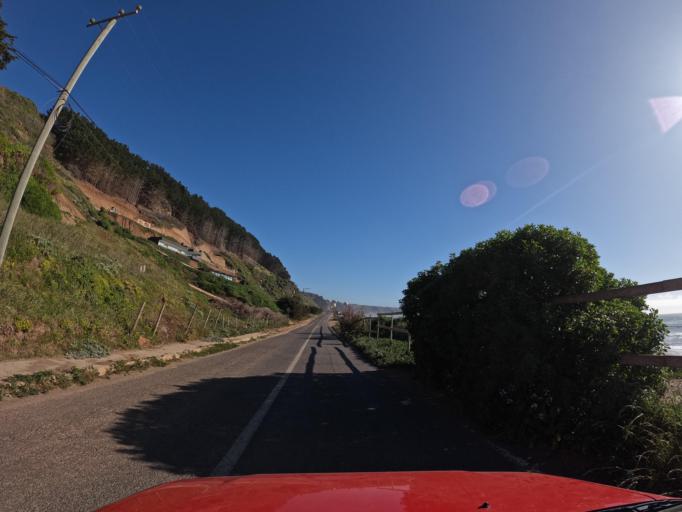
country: CL
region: Maule
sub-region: Provincia de Talca
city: Constitucion
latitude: -34.8595
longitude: -72.1465
